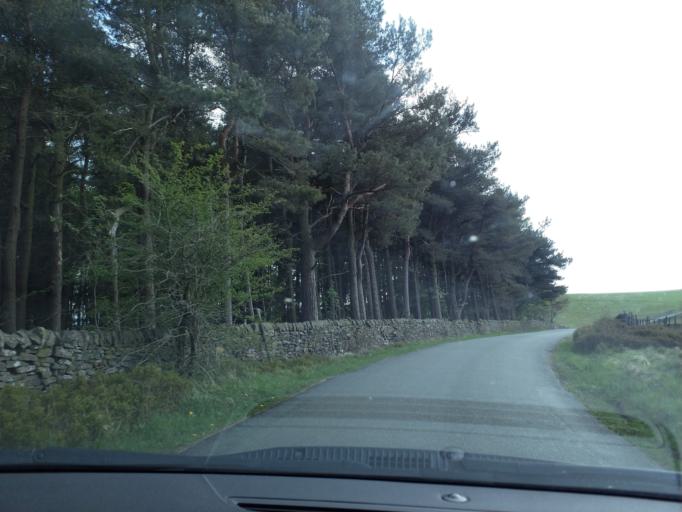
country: GB
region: England
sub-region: Derbyshire
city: Hathersage
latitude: 53.3543
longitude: -1.6604
